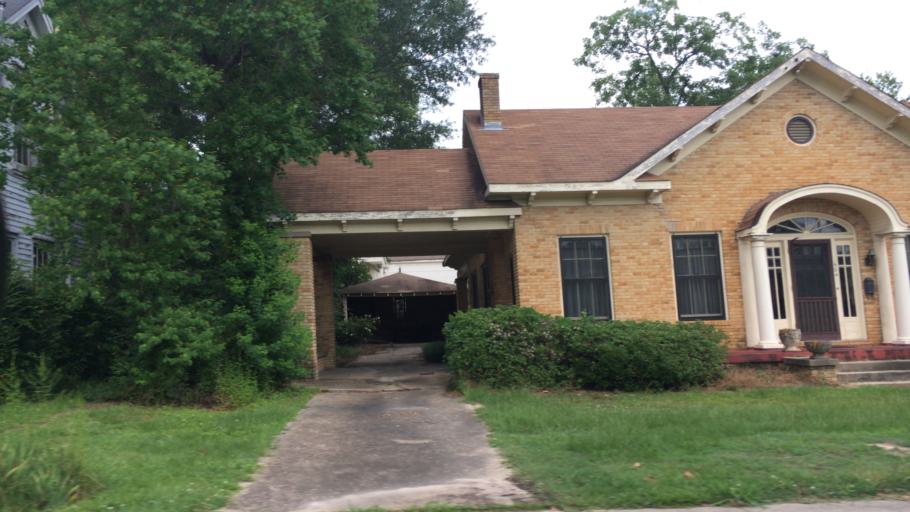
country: US
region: Louisiana
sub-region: Lincoln Parish
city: Ruston
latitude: 32.5330
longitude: -92.6389
